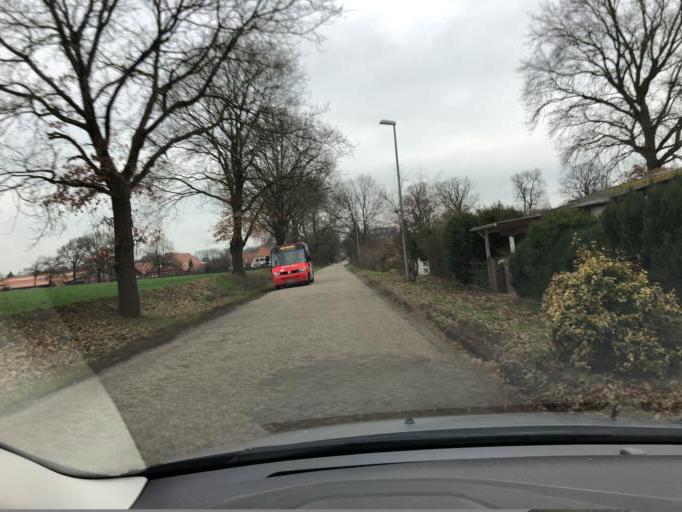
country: DE
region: Lower Saxony
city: Ganderkesee
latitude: 53.0939
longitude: 8.5677
